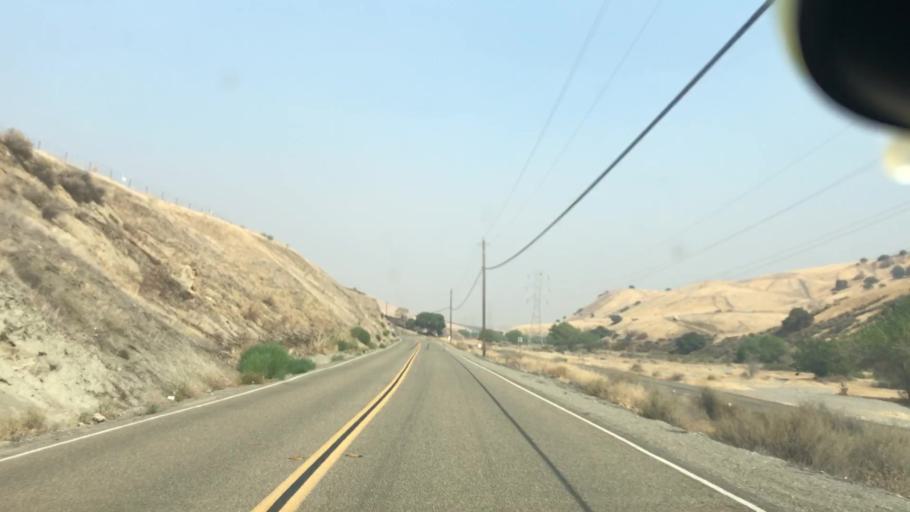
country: US
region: California
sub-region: San Joaquin County
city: Mountain House
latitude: 37.6369
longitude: -121.5631
